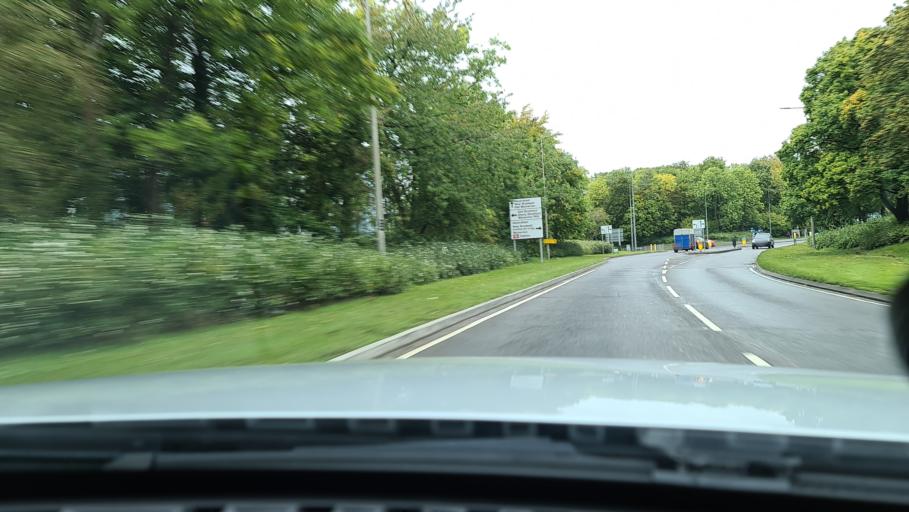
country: GB
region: England
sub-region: Milton Keynes
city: Stony Stratford
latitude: 52.0606
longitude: -0.8294
